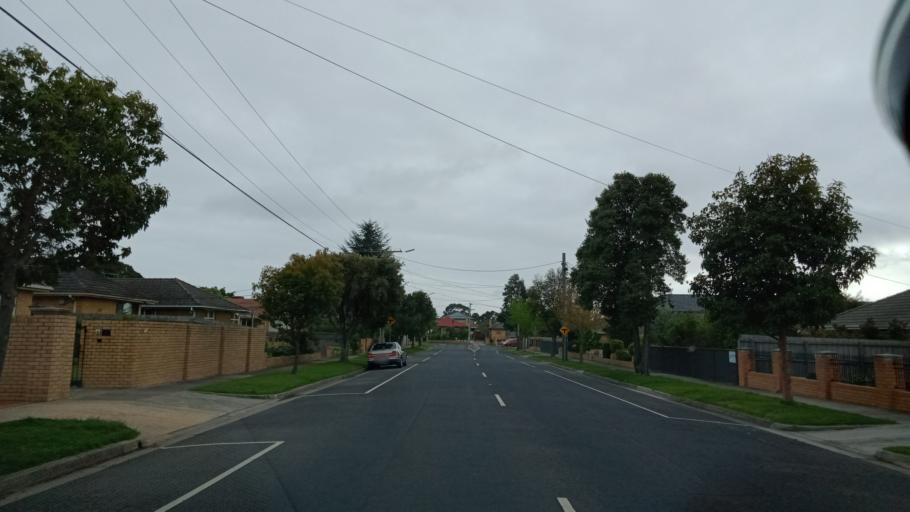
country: AU
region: Victoria
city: McKinnon
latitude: -37.9248
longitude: 145.0640
